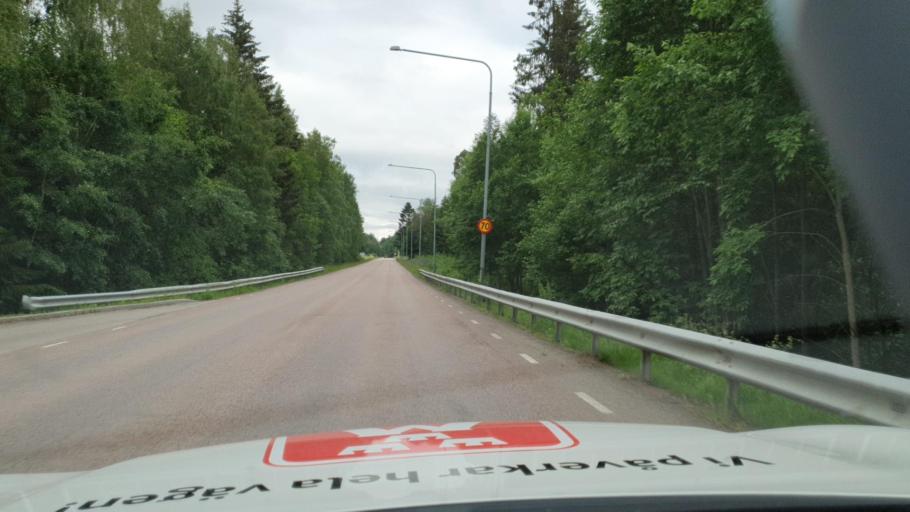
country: SE
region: Vaermland
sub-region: Kils Kommun
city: Kil
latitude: 59.5157
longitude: 13.3089
